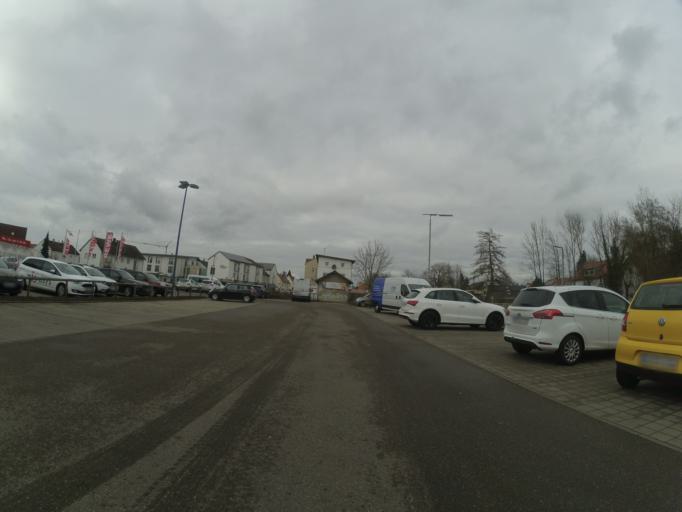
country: DE
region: Bavaria
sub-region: Swabia
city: Senden
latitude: 48.3229
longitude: 10.0511
